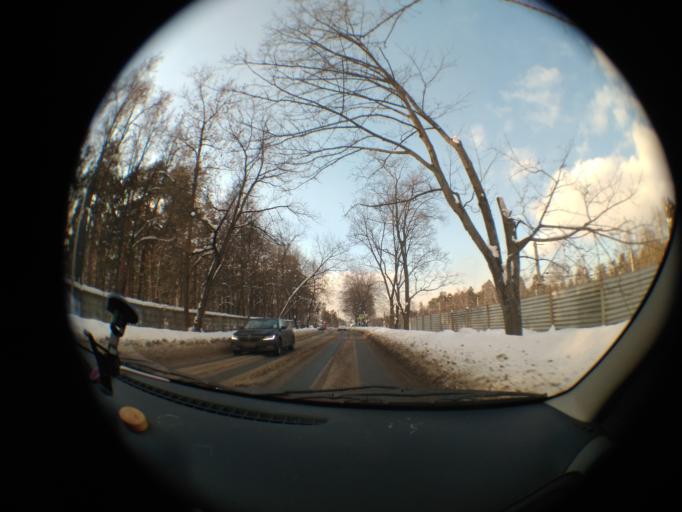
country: RU
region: Moskovskaya
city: Il'inskiy
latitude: 55.6136
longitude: 38.1065
